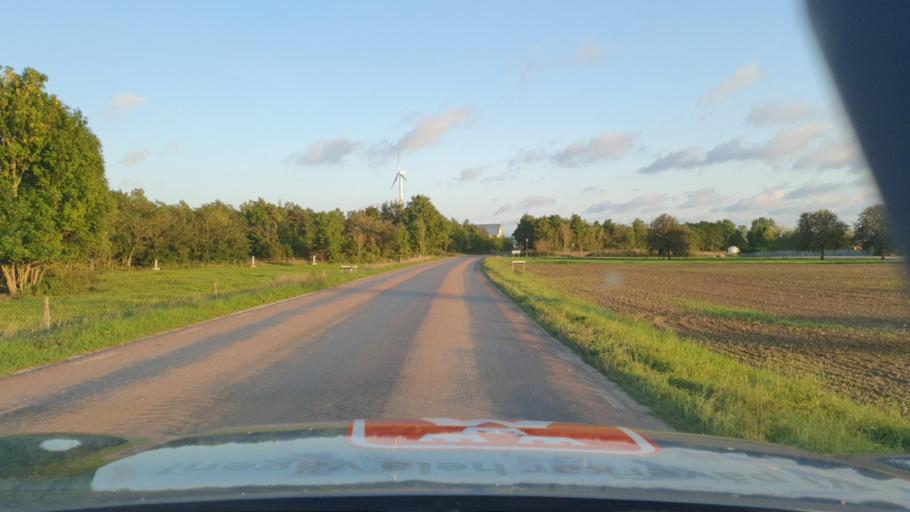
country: SE
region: Gotland
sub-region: Gotland
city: Visby
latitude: 57.6505
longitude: 18.5492
